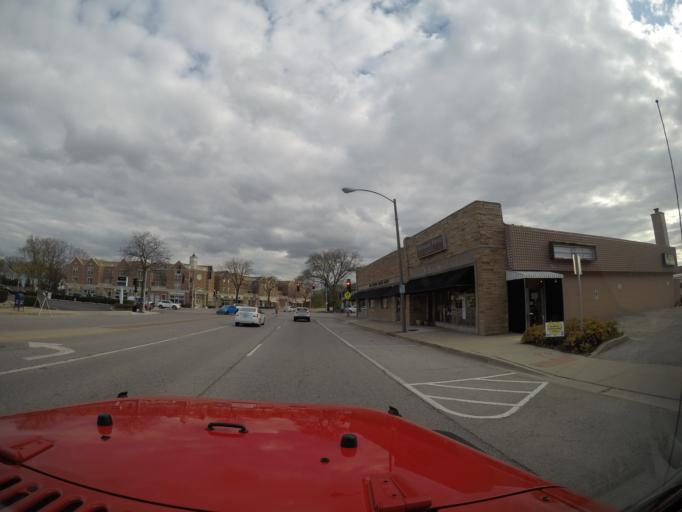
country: US
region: Illinois
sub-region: Cook County
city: Glenview
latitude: 42.0733
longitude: -87.7990
